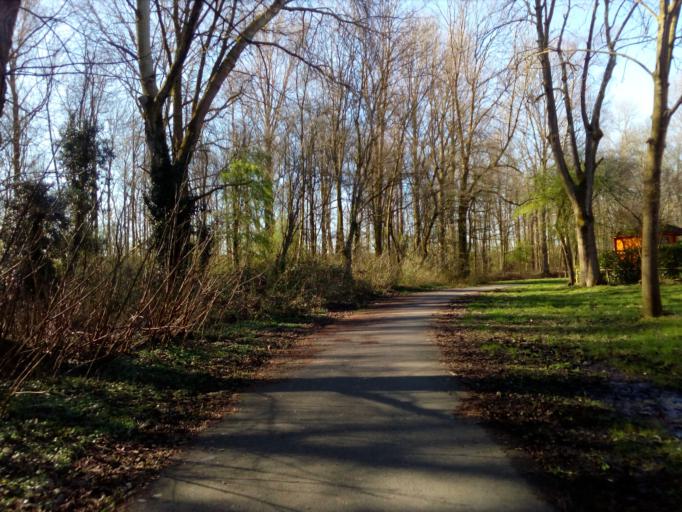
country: NL
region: South Holland
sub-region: Gemeente Zoetermeer
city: Zoetermeer
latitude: 52.0506
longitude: 4.4662
